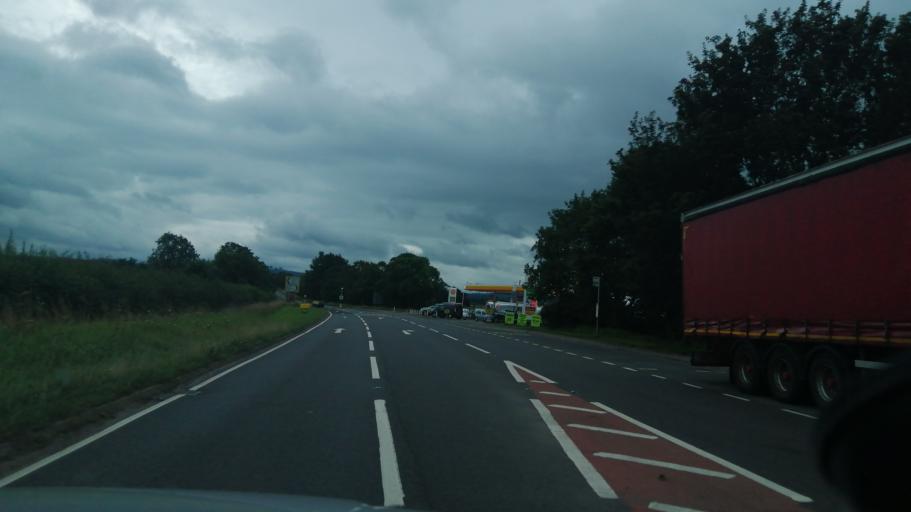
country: GB
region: England
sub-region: Herefordshire
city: Thruxton
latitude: 52.0010
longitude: -2.7930
